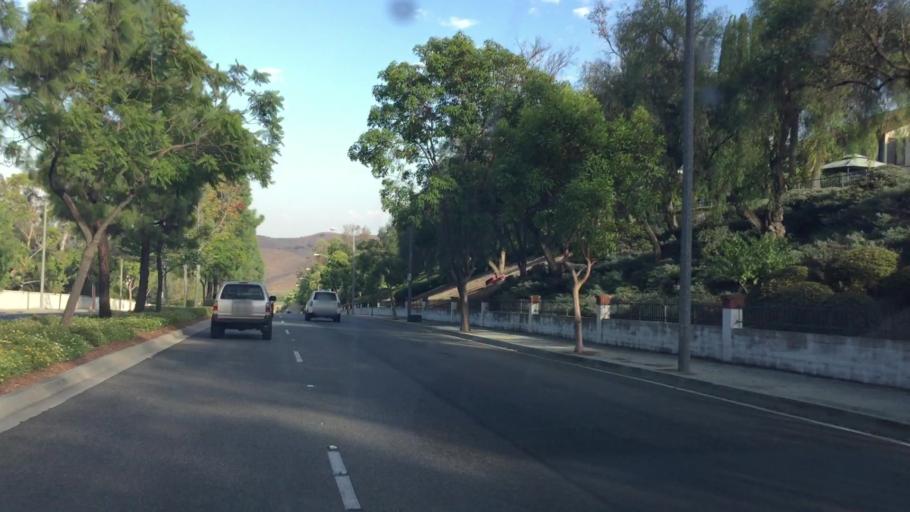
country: US
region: California
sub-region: Los Angeles County
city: Diamond Bar
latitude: 33.9957
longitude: -117.7968
